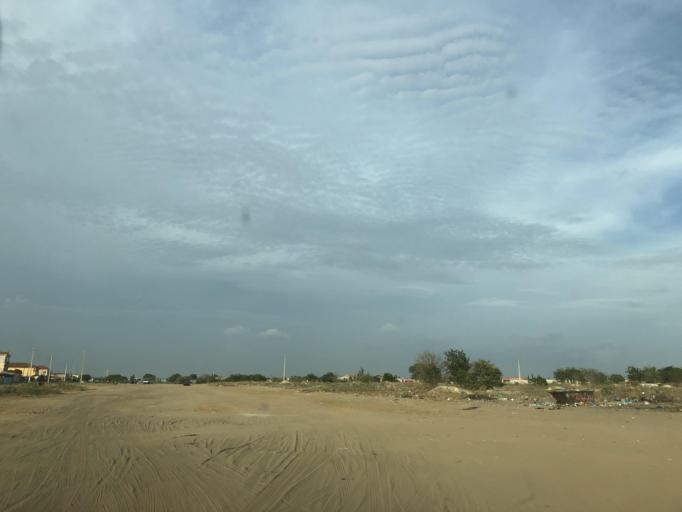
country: AO
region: Luanda
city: Luanda
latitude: -8.9137
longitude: 13.3133
